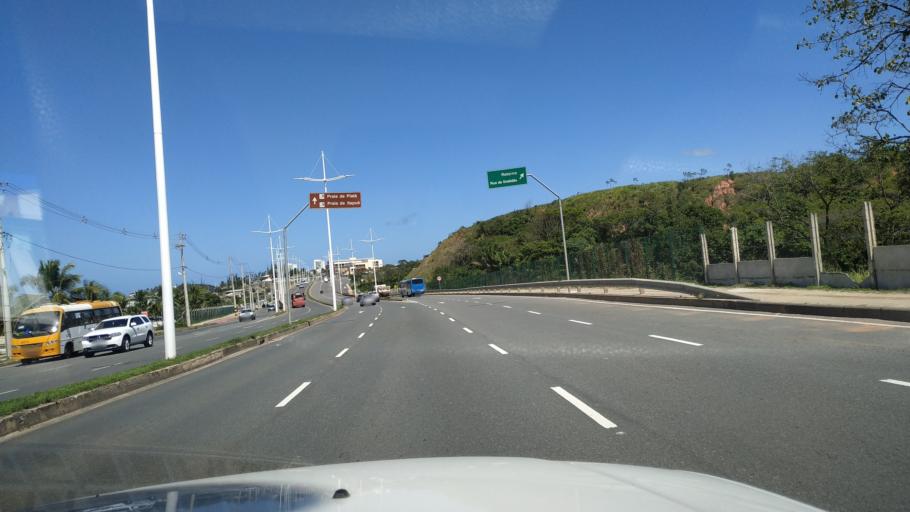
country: BR
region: Bahia
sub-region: Lauro De Freitas
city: Lauro de Freitas
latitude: -12.9341
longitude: -38.3846
